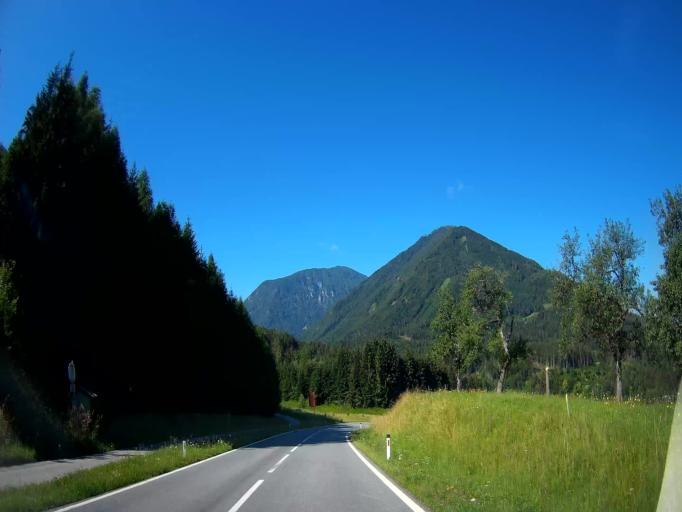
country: AT
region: Carinthia
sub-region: Politischer Bezirk Volkermarkt
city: Gallizien
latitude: 46.5340
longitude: 14.4633
